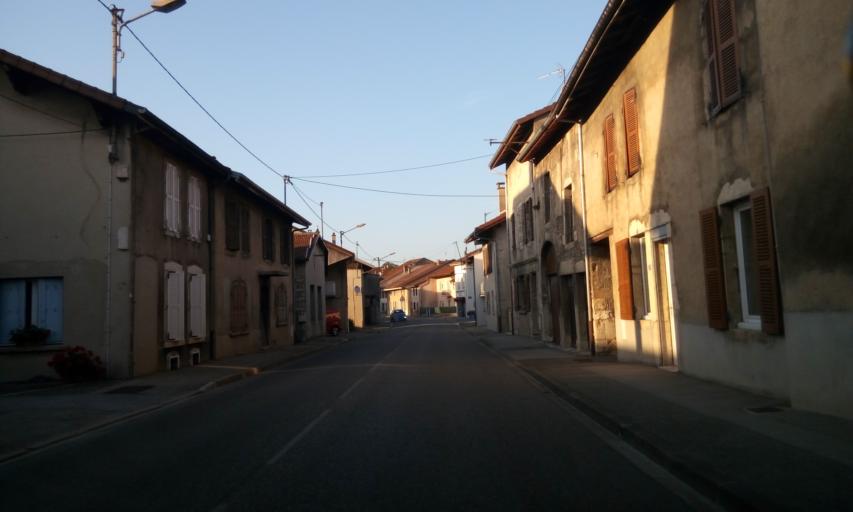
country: FR
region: Rhone-Alpes
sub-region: Departement de l'Ain
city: Saint-Martin-du-Frene
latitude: 46.1381
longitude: 5.5524
